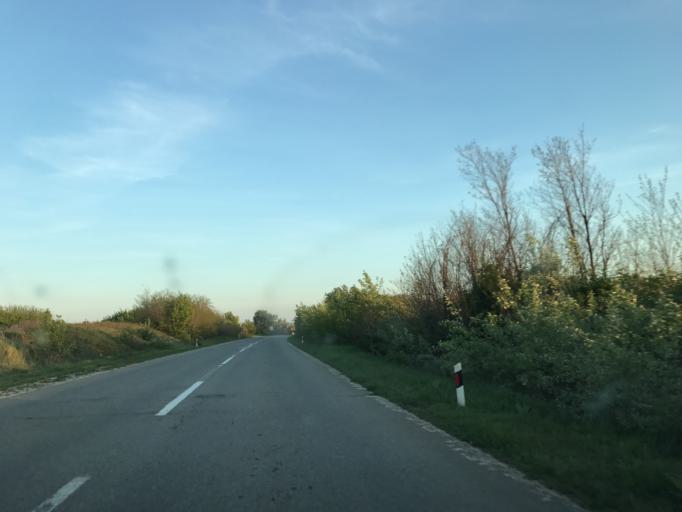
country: RO
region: Mehedinti
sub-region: Comuna Gogosu
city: Ostrovu Mare
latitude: 44.3793
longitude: 22.4790
